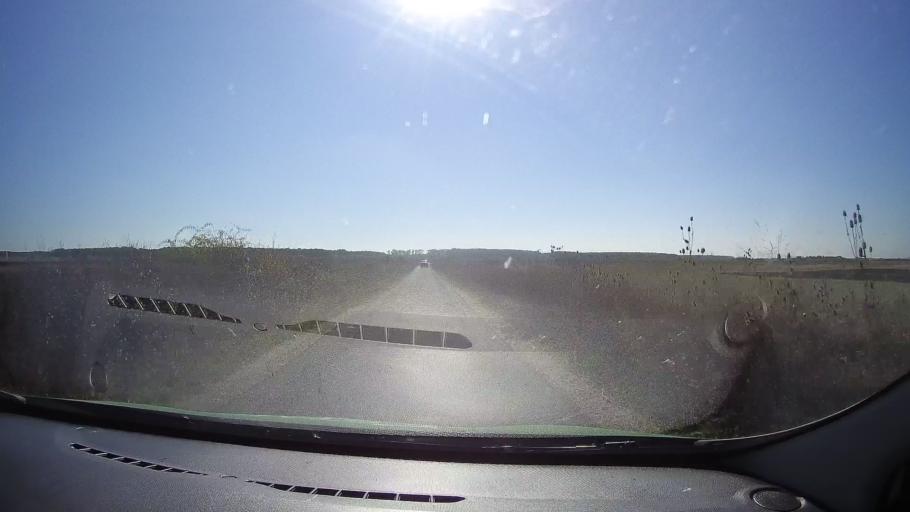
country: RO
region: Satu Mare
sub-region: Comuna Doba
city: Doba
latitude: 47.7256
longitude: 22.7243
